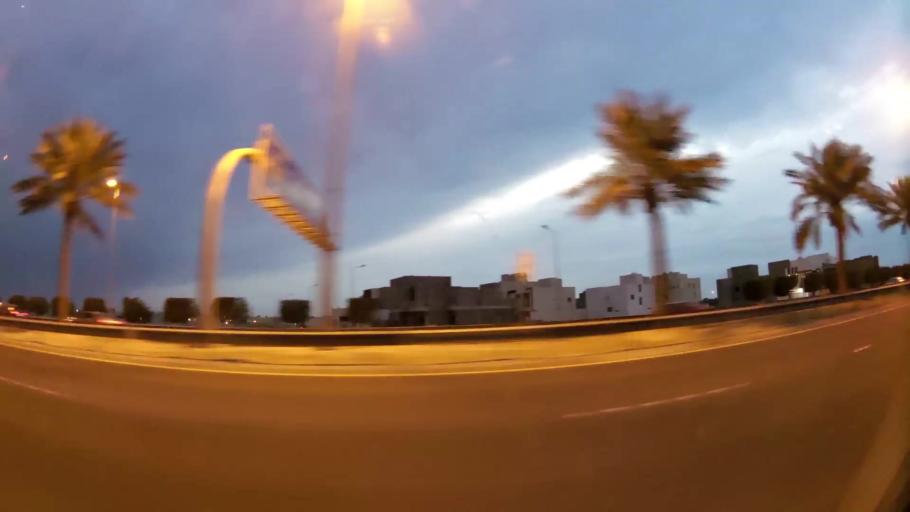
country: BH
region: Central Governorate
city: Madinat Hamad
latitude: 26.1502
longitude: 50.5086
